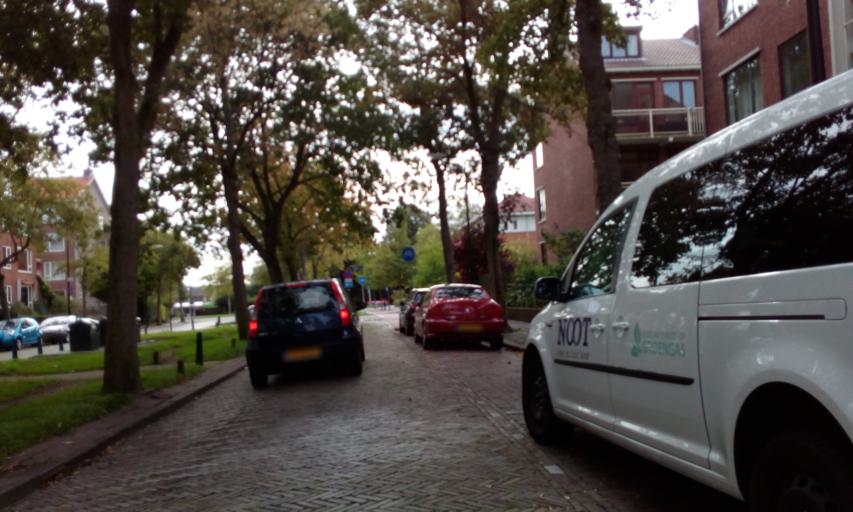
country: NL
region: South Holland
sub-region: Gemeente Rijswijk
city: Rijswijk
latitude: 52.0491
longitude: 4.3357
